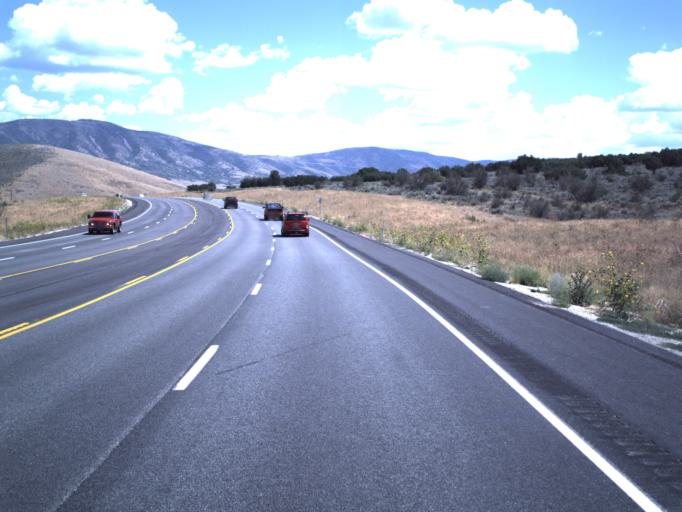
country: US
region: Utah
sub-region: Wasatch County
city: Midway
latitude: 40.4063
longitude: -111.4916
